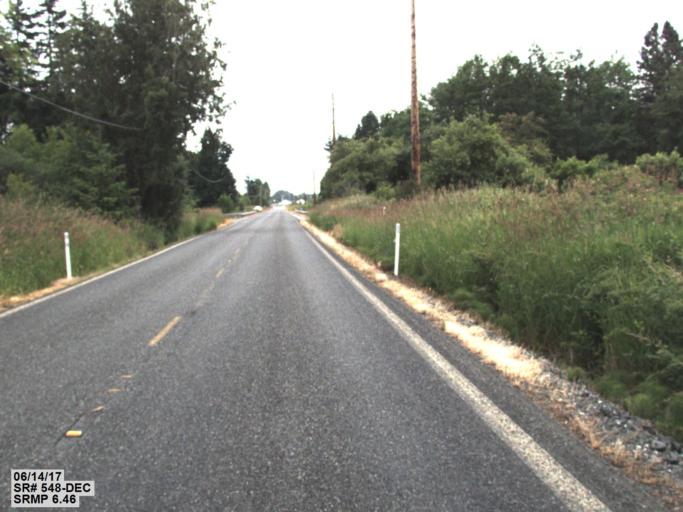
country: US
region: Washington
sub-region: Whatcom County
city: Birch Bay
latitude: 48.8997
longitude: -122.7266
